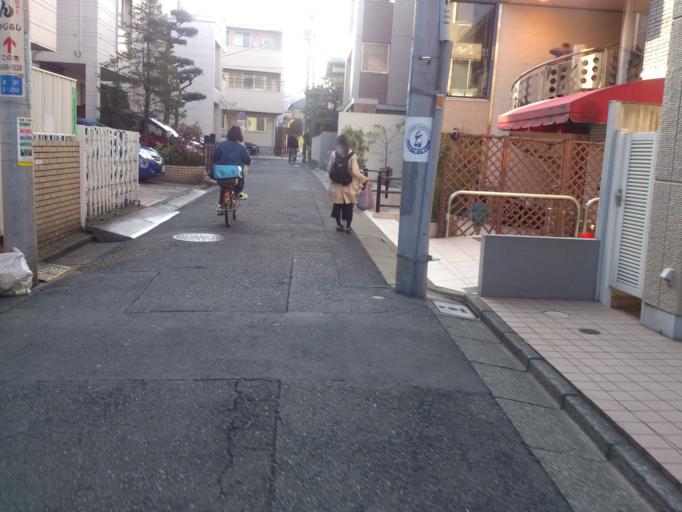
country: JP
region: Tokyo
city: Tokyo
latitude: 35.6634
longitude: 139.6671
